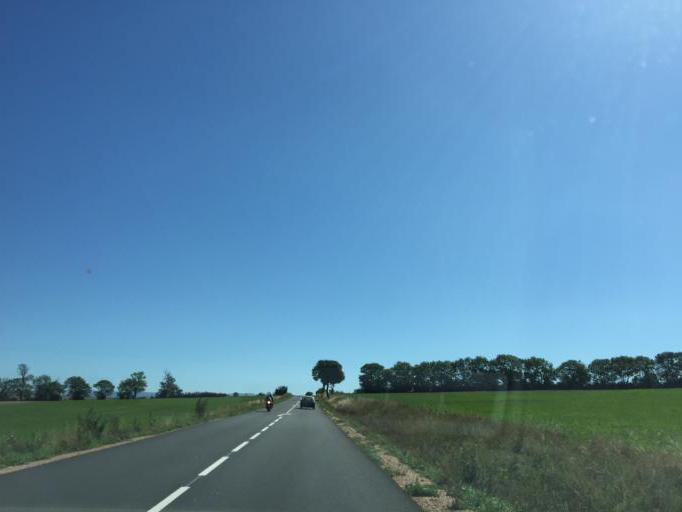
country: FR
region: Midi-Pyrenees
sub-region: Departement de l'Aveyron
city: La Cavalerie
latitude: 44.0155
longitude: 3.0930
